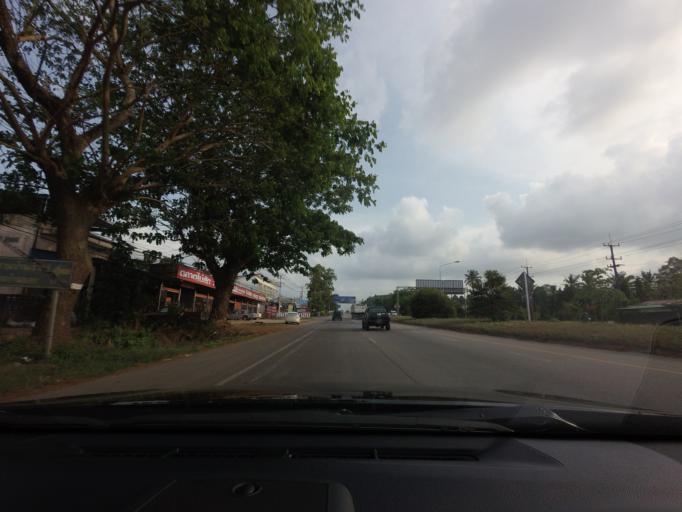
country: TH
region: Chumphon
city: Lang Suan
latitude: 9.9766
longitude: 99.0683
